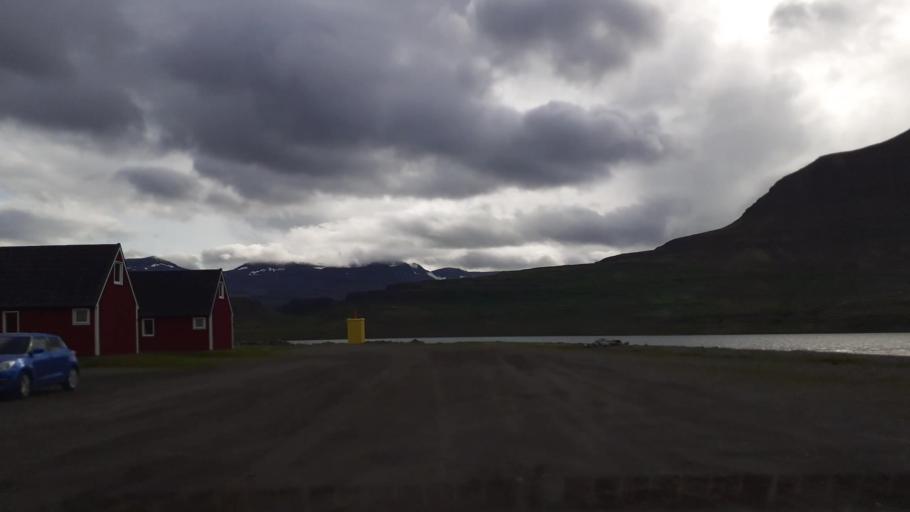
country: IS
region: East
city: Eskifjoerdur
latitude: 65.0602
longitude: -13.9927
